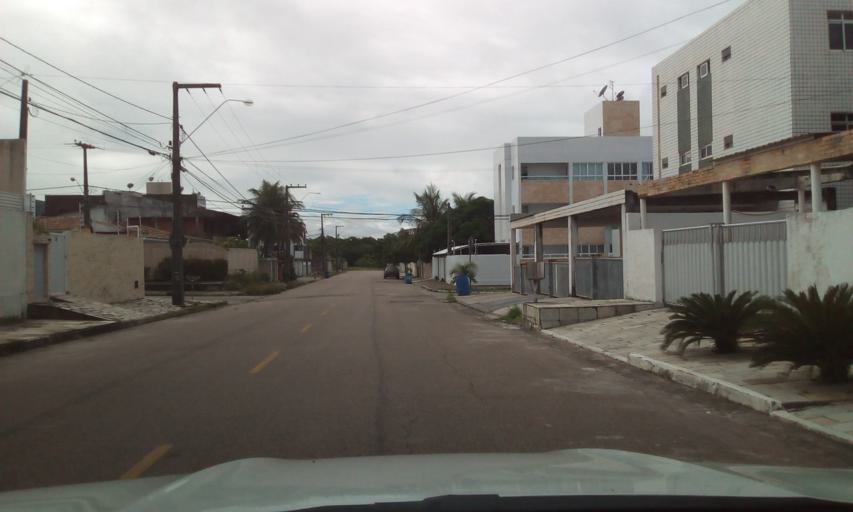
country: BR
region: Paraiba
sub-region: Joao Pessoa
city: Joao Pessoa
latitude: -7.0612
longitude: -34.8463
